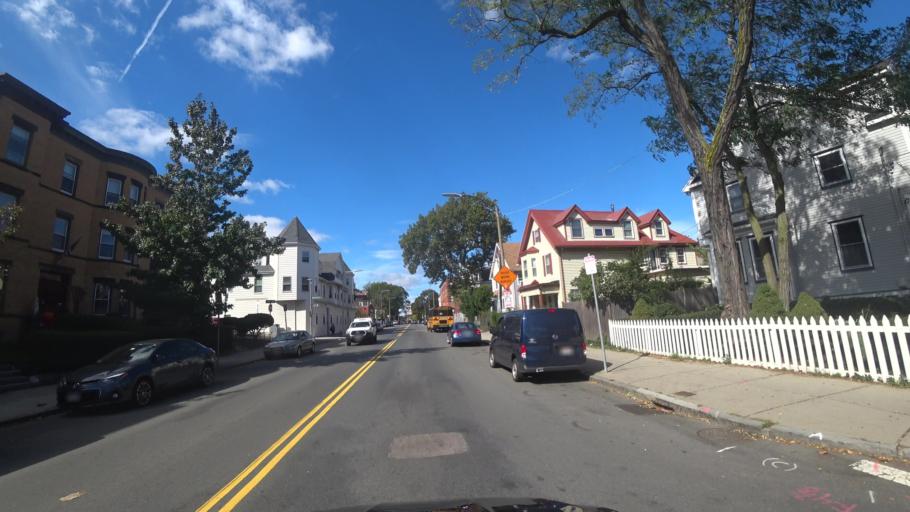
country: US
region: Massachusetts
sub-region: Suffolk County
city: South Boston
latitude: 42.3153
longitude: -71.0613
